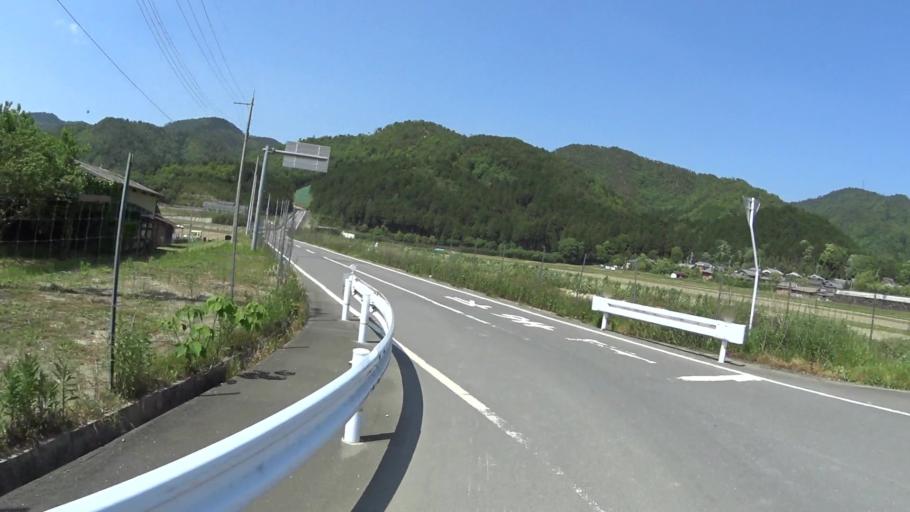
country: JP
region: Kyoto
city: Kameoka
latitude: 35.0913
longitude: 135.5515
